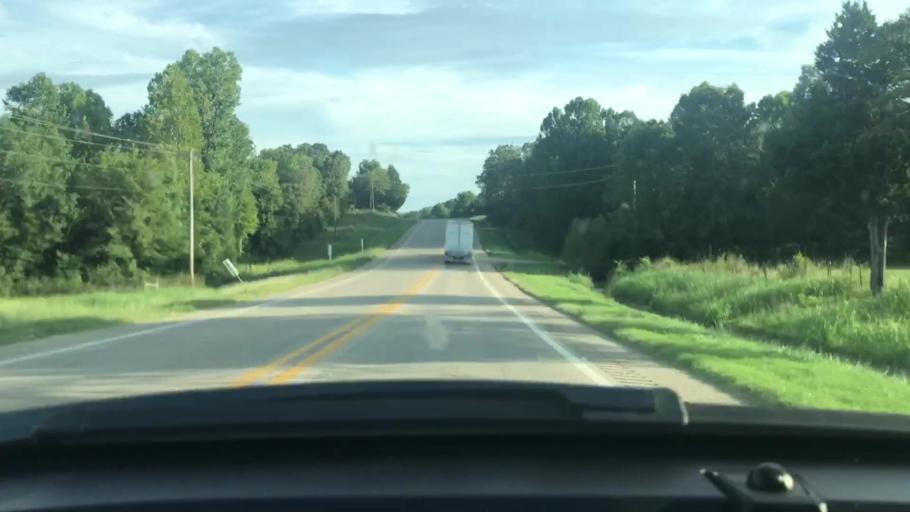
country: US
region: Arkansas
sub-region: Lawrence County
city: Hoxie
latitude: 36.1578
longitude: -91.1619
